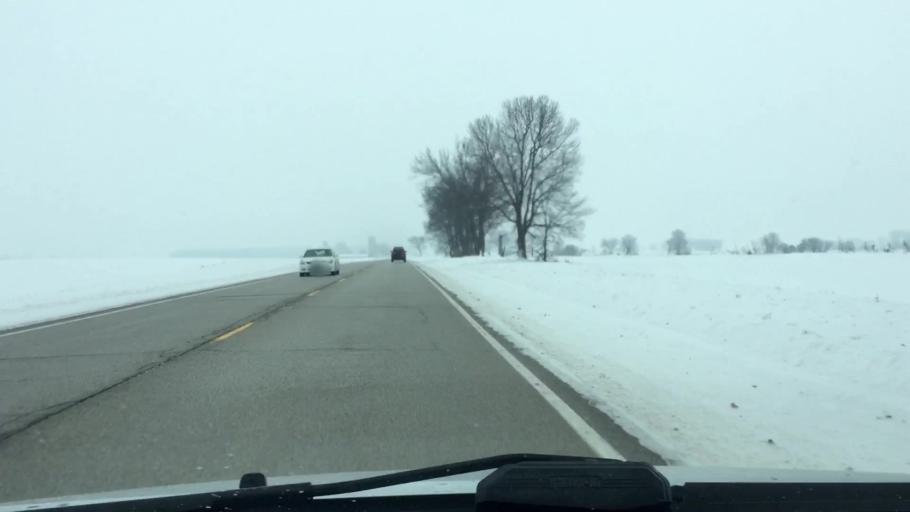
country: US
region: Illinois
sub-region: McHenry County
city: Hebron
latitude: 42.4367
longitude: -88.4383
